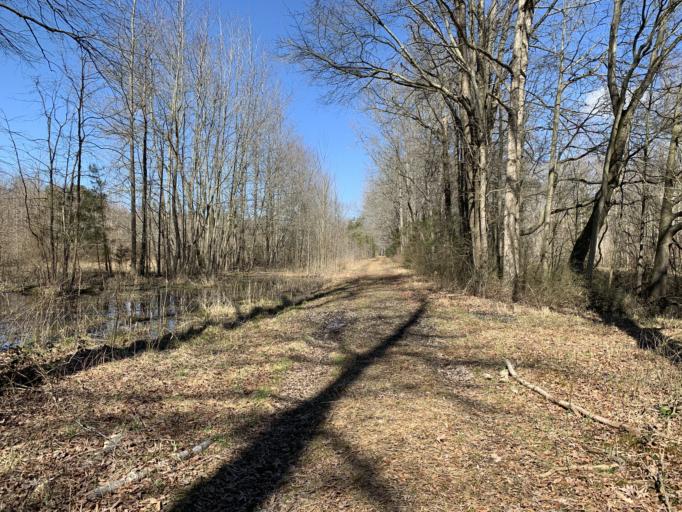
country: US
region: Delaware
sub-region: Kent County
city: Felton
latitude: 39.0427
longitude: -75.5990
